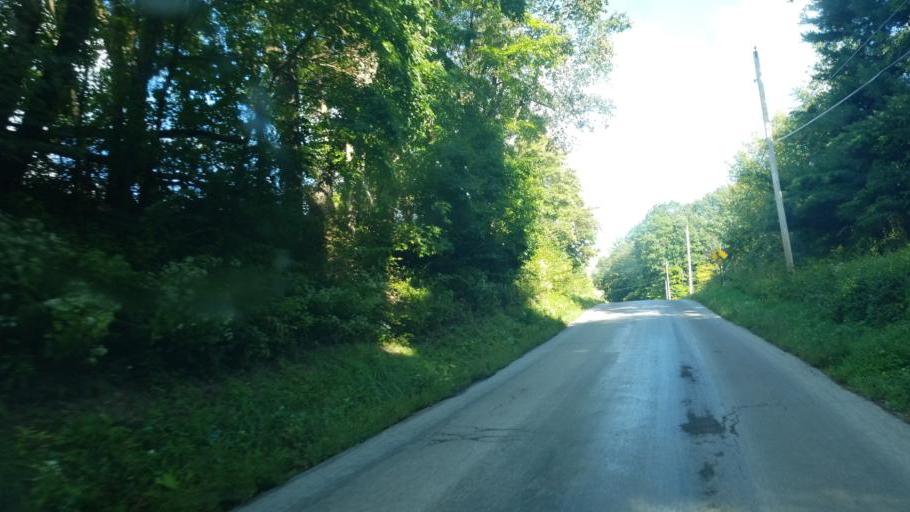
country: US
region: Ohio
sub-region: Sandusky County
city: Bellville
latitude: 40.5864
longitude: -82.5696
